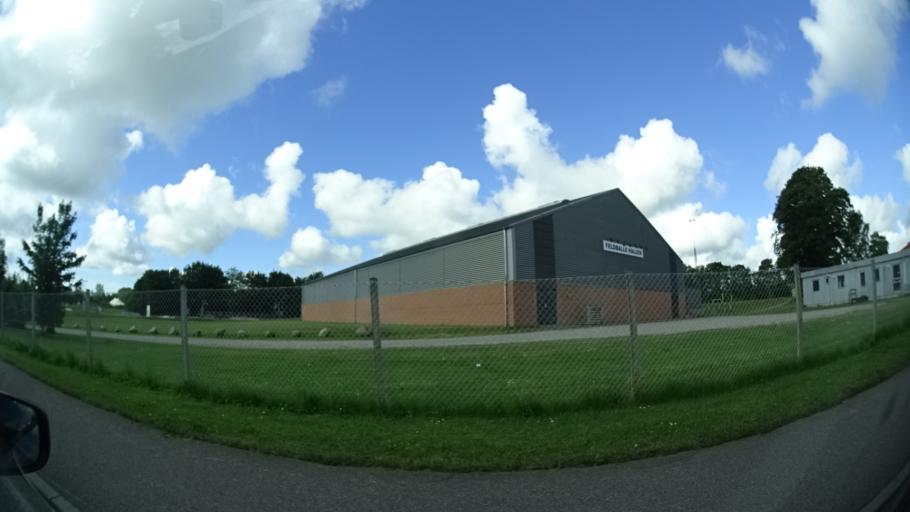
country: DK
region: Central Jutland
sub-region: Syddjurs Kommune
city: Ronde
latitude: 56.2836
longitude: 10.5869
